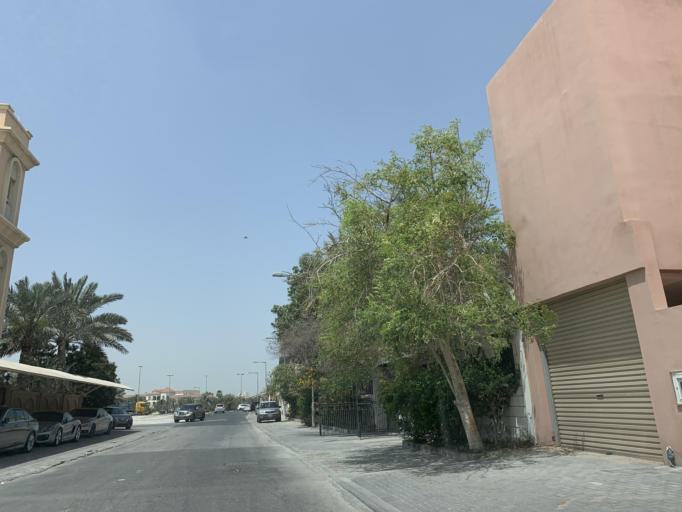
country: BH
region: Manama
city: Jidd Hafs
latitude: 26.1986
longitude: 50.5602
